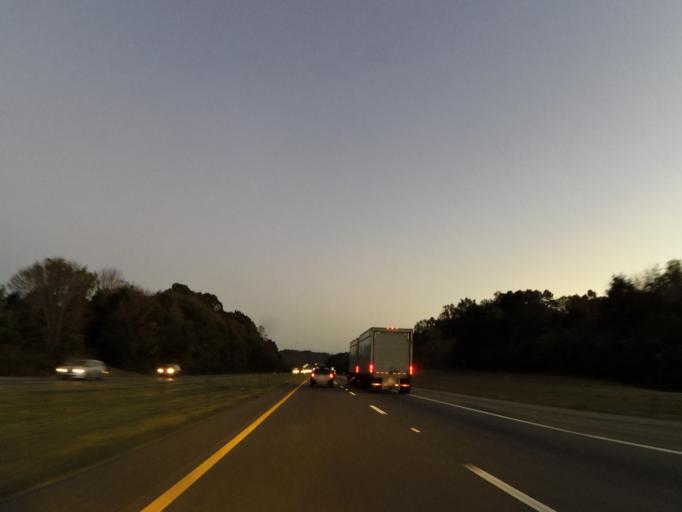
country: US
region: Tennessee
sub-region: Anderson County
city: Clinton
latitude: 36.0639
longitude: -84.0092
